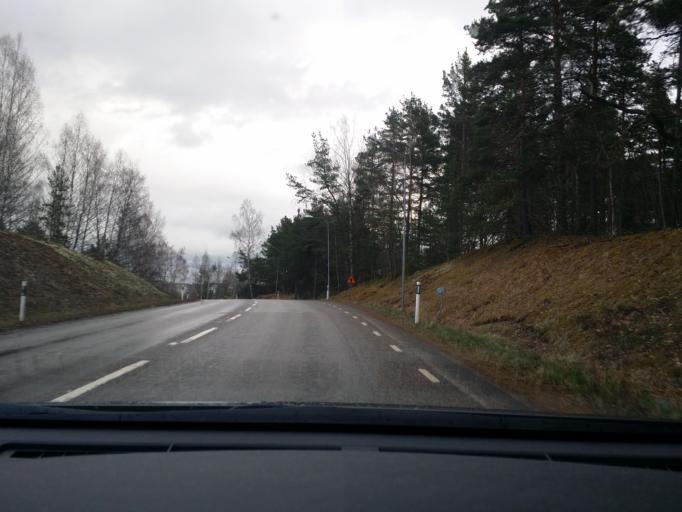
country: SE
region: Soedermanland
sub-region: Eskilstuna Kommun
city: Arla
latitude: 59.3827
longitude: 16.6716
